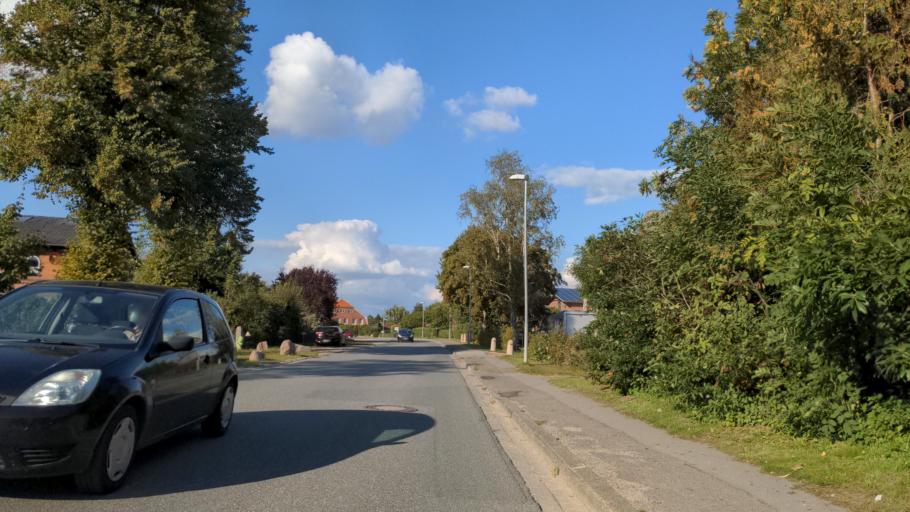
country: DE
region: Schleswig-Holstein
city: Monkhagen
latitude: 53.9386
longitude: 10.5982
